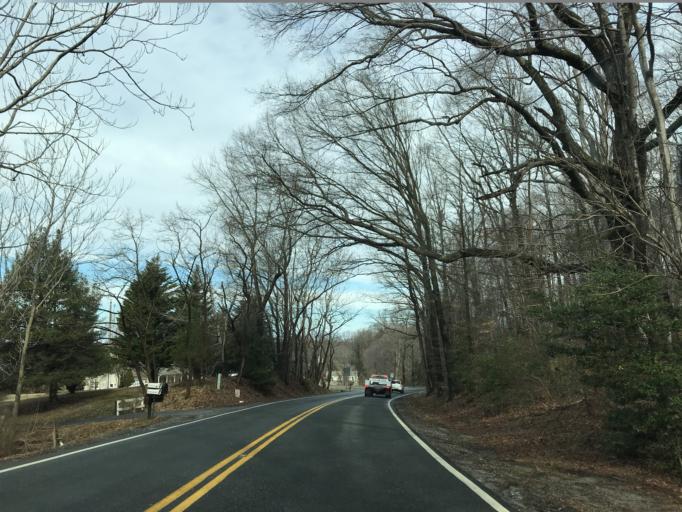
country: US
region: Virginia
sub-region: King George County
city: Dahlgren
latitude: 38.2826
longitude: -77.0467
